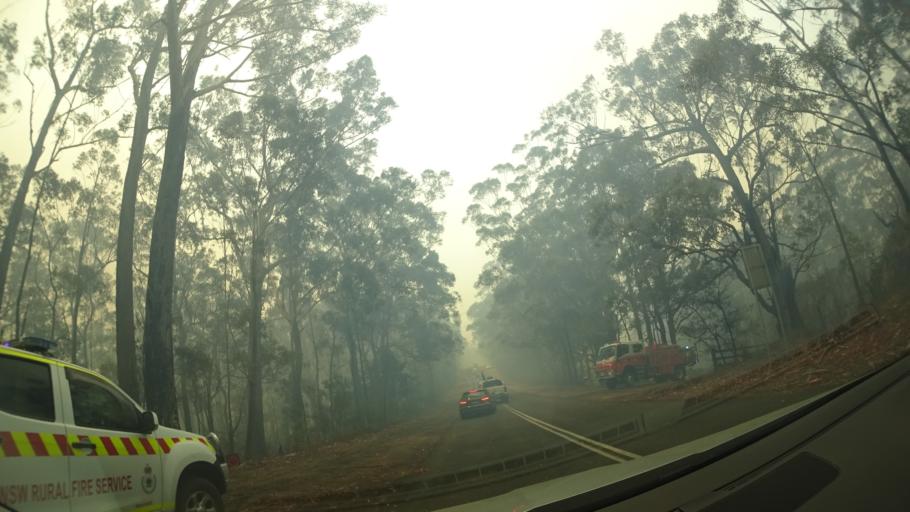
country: AU
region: New South Wales
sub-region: Shoalhaven Shire
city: Milton
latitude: -35.2117
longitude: 150.4597
